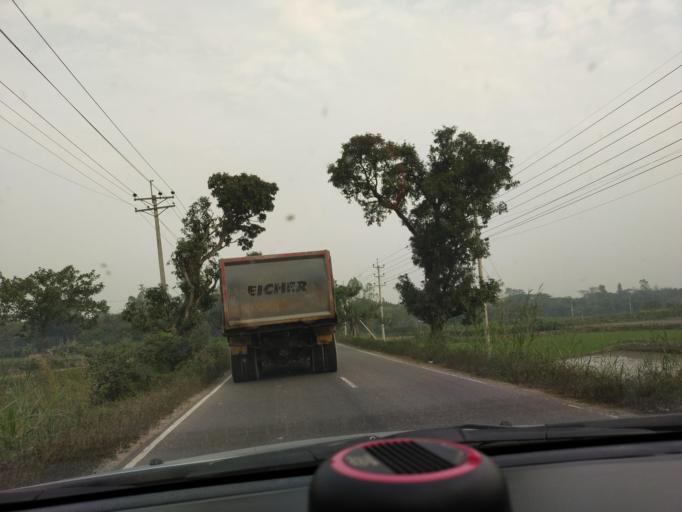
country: BD
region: Dhaka
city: Narsingdi
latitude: 24.0192
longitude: 90.7377
